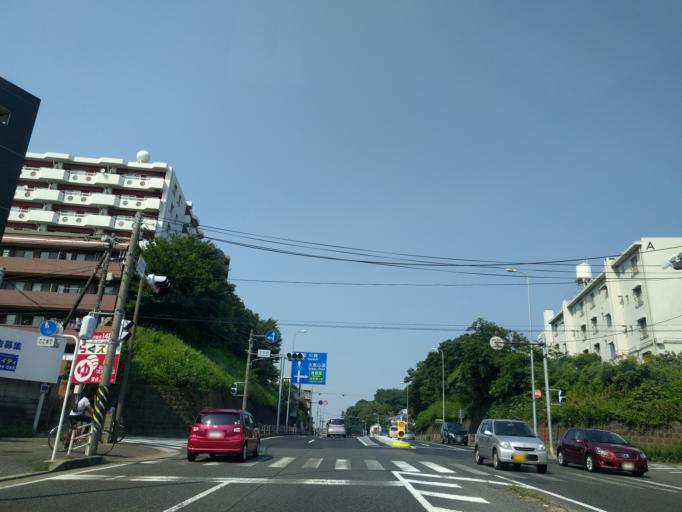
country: JP
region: Kanagawa
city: Yokohama
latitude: 35.4931
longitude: 139.6564
